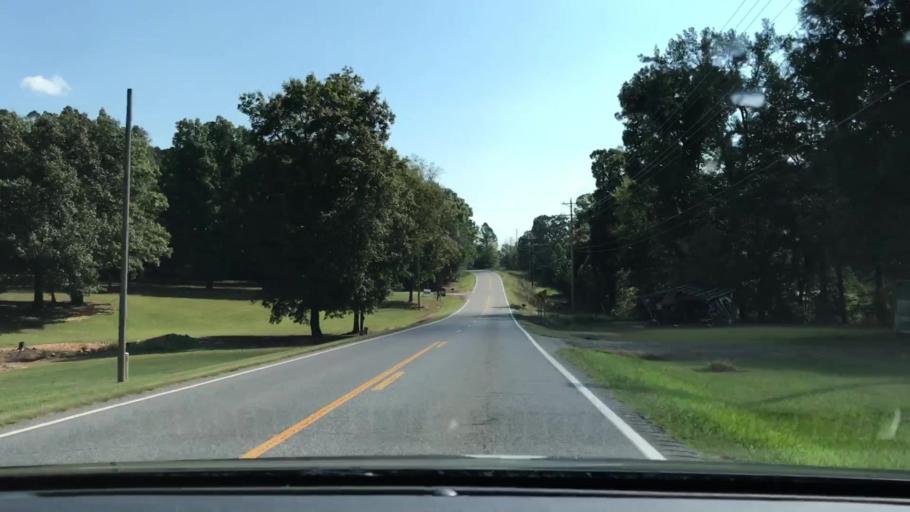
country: US
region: Kentucky
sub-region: Marshall County
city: Benton
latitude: 36.7651
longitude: -88.2633
